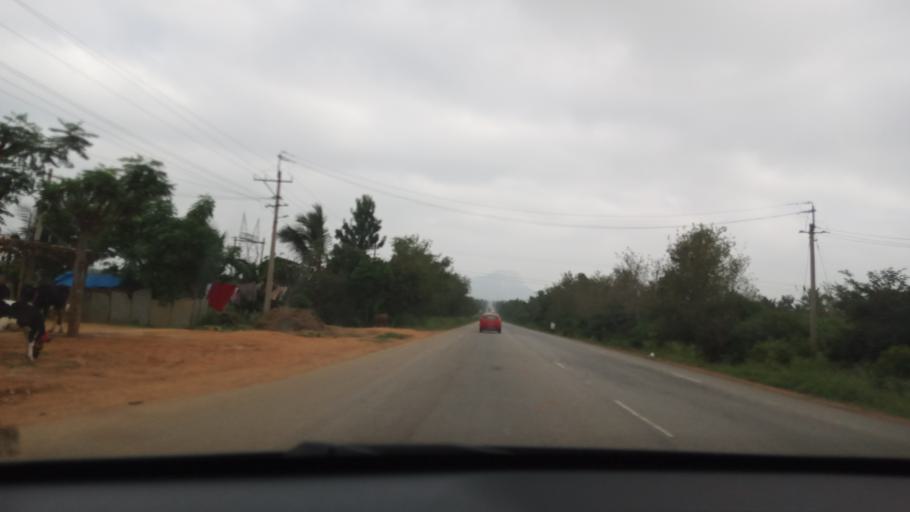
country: IN
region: Karnataka
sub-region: Chikkaballapur
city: Chintamani
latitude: 13.2944
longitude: 77.9664
